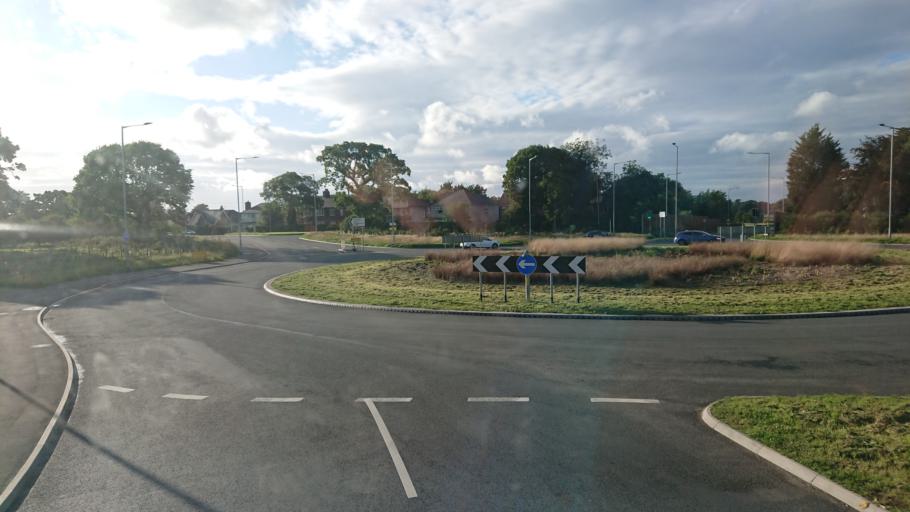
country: GB
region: England
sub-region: Lancashire
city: Preston
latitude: 53.8109
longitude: -2.7177
